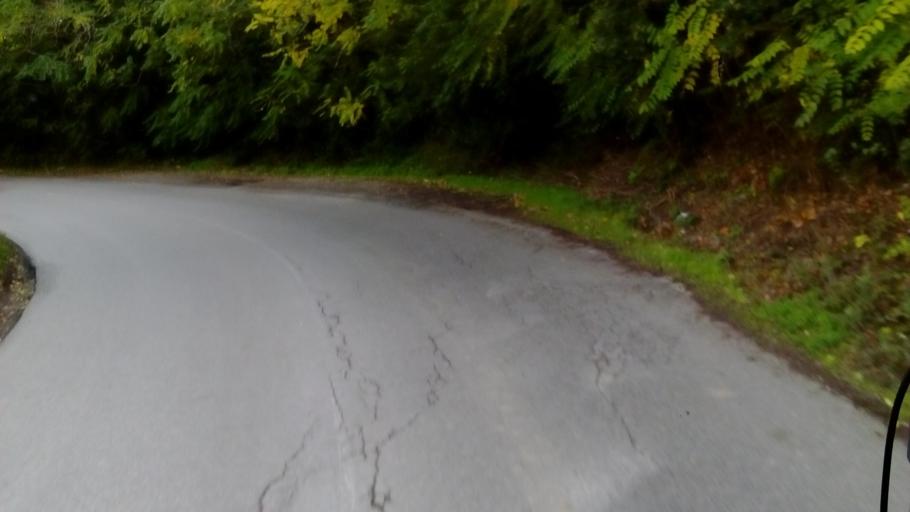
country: IT
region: Tuscany
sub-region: Province of Florence
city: Montespertoli
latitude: 43.6497
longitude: 11.0847
